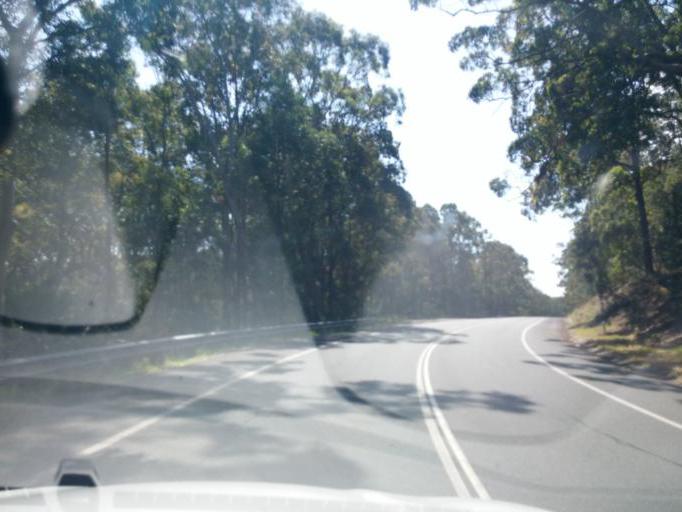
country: AU
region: New South Wales
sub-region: Great Lakes
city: Forster
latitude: -32.3144
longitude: 152.5115
